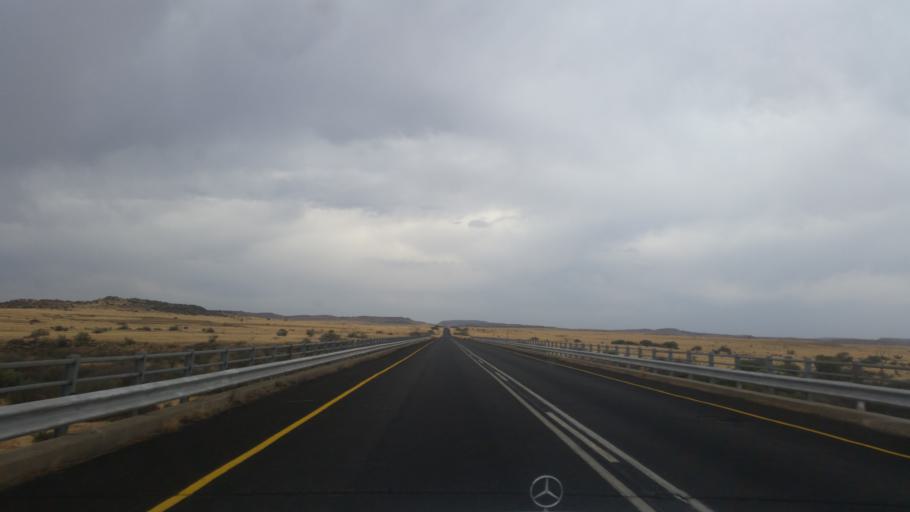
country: ZA
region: Orange Free State
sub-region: Xhariep District Municipality
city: Trompsburg
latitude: -30.4260
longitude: 26.1099
